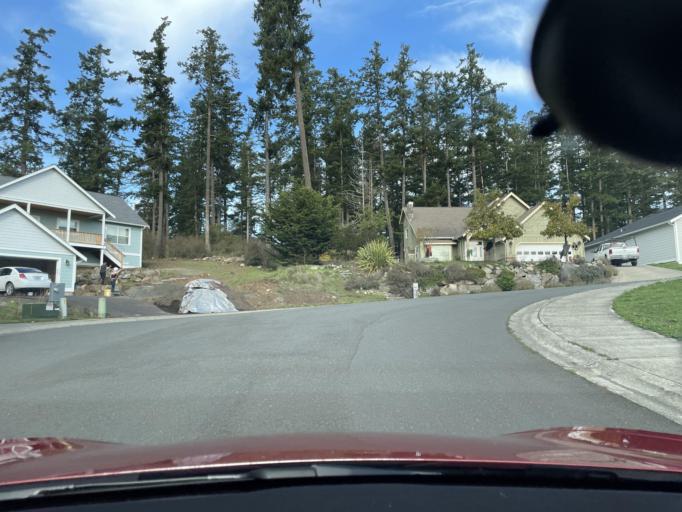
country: US
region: Washington
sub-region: San Juan County
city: Friday Harbor
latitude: 48.5429
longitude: -123.0334
